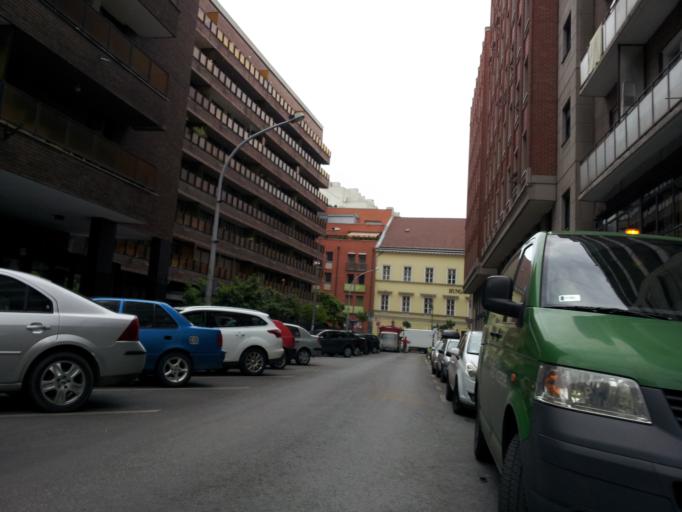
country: HU
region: Budapest
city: Budapest VI. keruelet
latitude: 47.4985
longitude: 19.0580
